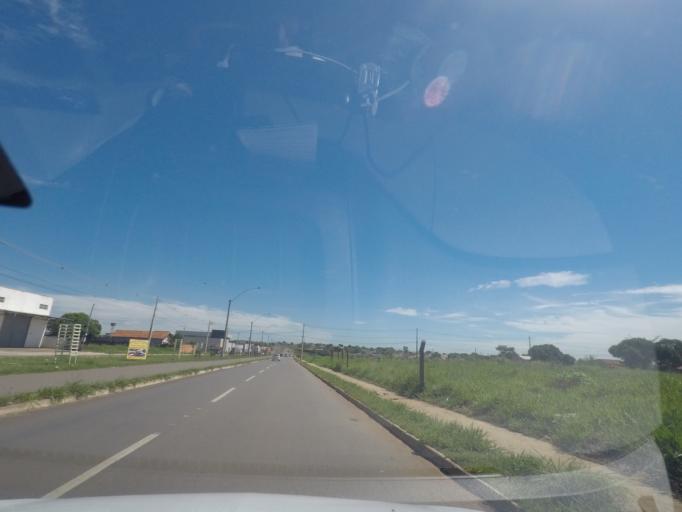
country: BR
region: Goias
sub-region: Aparecida De Goiania
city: Aparecida de Goiania
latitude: -16.8009
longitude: -49.3286
